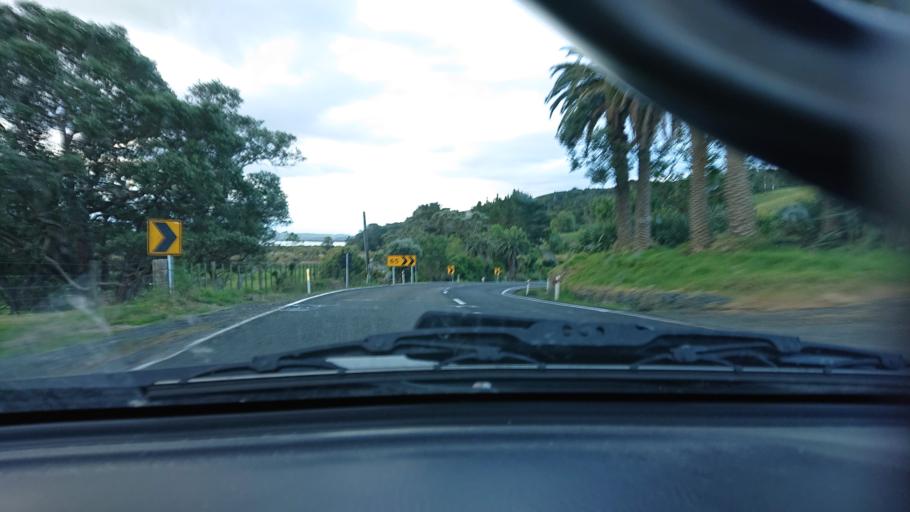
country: NZ
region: Auckland
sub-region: Auckland
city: Wellsford
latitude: -36.4402
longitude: 174.4321
